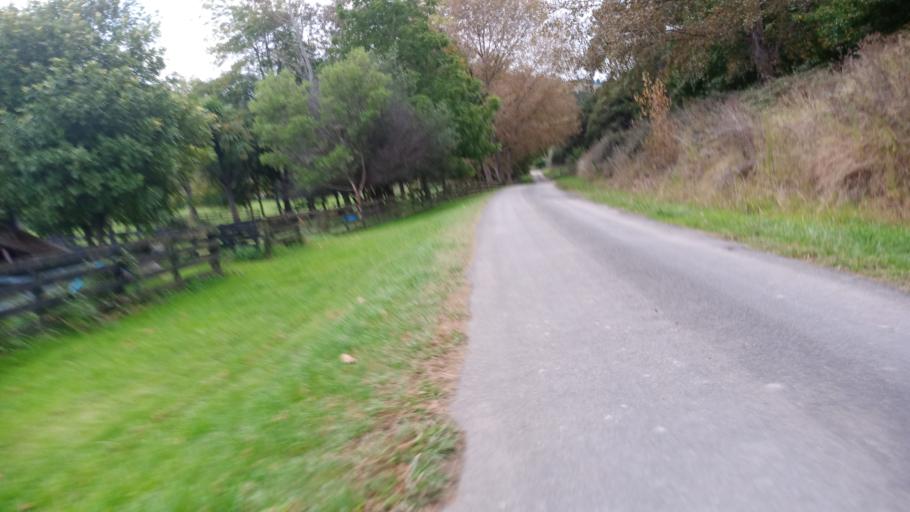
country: NZ
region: Gisborne
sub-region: Gisborne District
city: Gisborne
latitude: -38.6451
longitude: 178.0341
